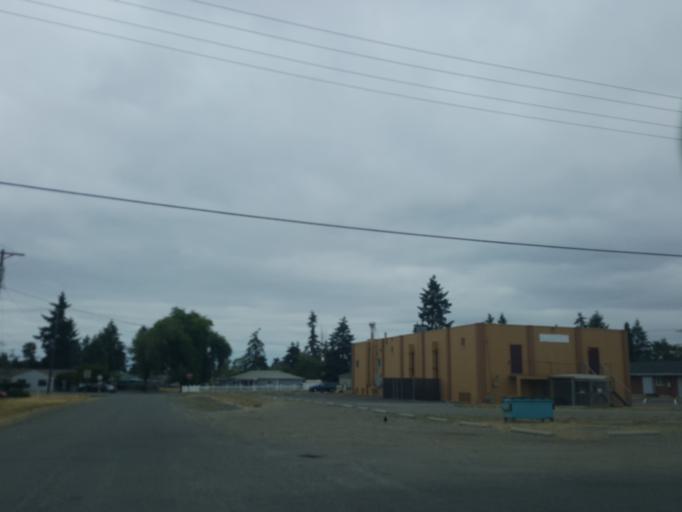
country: US
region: Washington
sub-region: Pierce County
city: Lakewood
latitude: 47.1584
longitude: -122.5023
